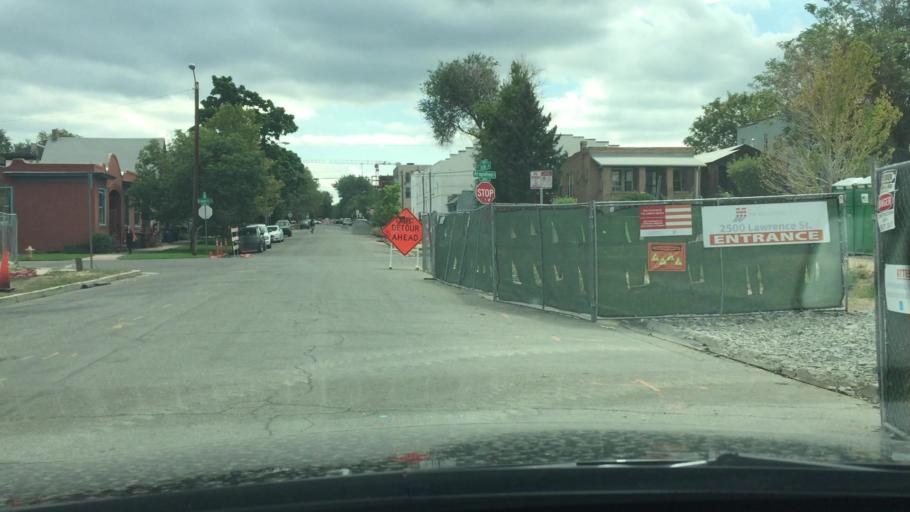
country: US
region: Colorado
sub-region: Denver County
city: Denver
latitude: 39.7575
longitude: -104.9839
